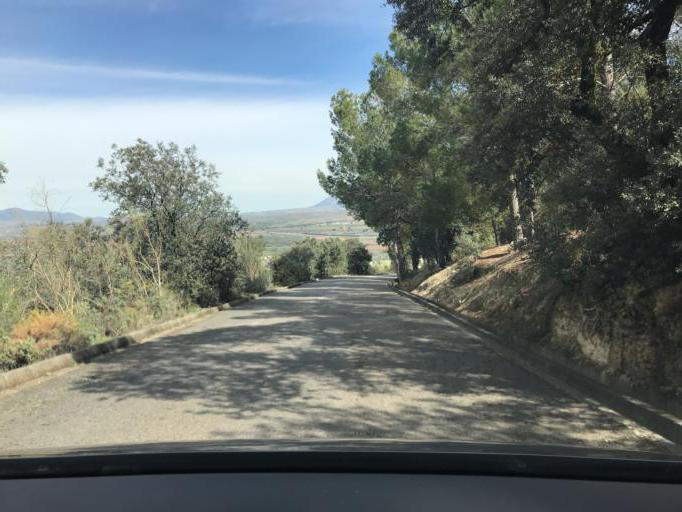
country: ES
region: Andalusia
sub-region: Provincia de Granada
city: Atarfe
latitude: 37.2495
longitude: -3.6809
